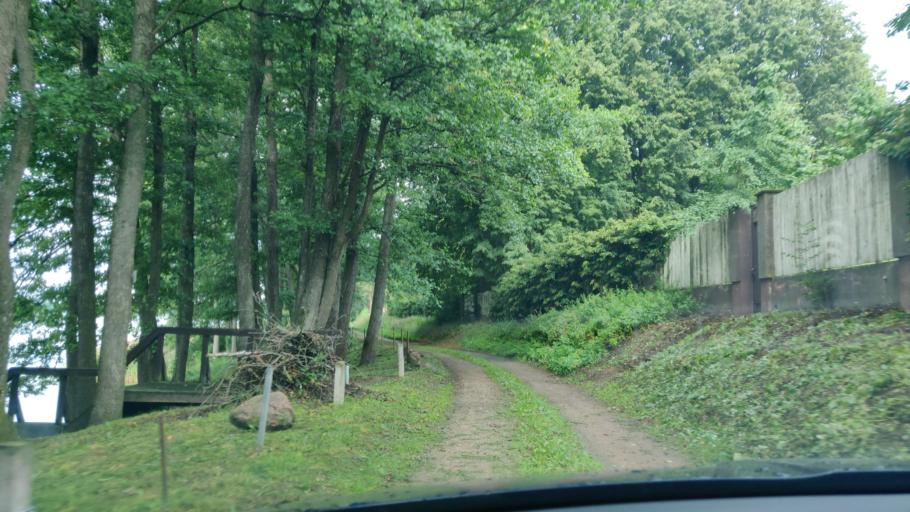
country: LT
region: Vilnius County
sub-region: Trakai
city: Rudiskes
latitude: 54.6096
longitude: 24.8347
